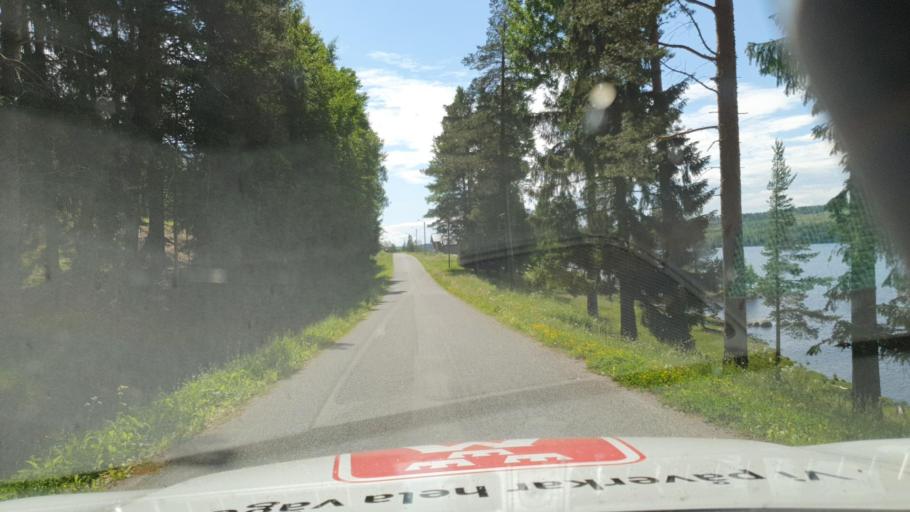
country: SE
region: Jaemtland
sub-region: Bergs Kommun
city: Hoverberg
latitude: 62.8412
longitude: 14.4108
